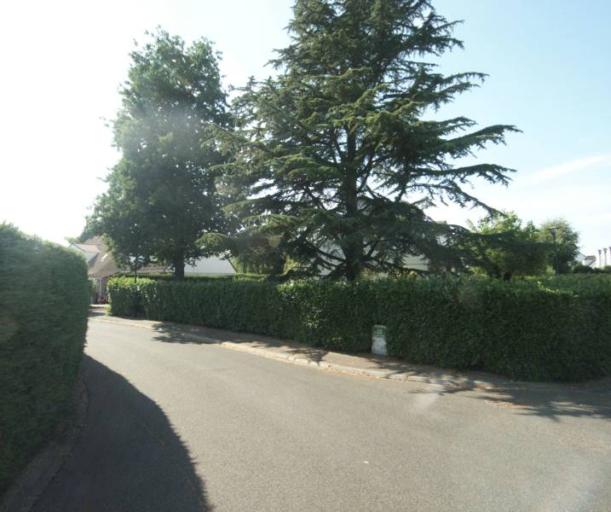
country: FR
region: Nord-Pas-de-Calais
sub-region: Departement du Nord
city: Bondues
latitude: 50.7043
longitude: 3.0734
